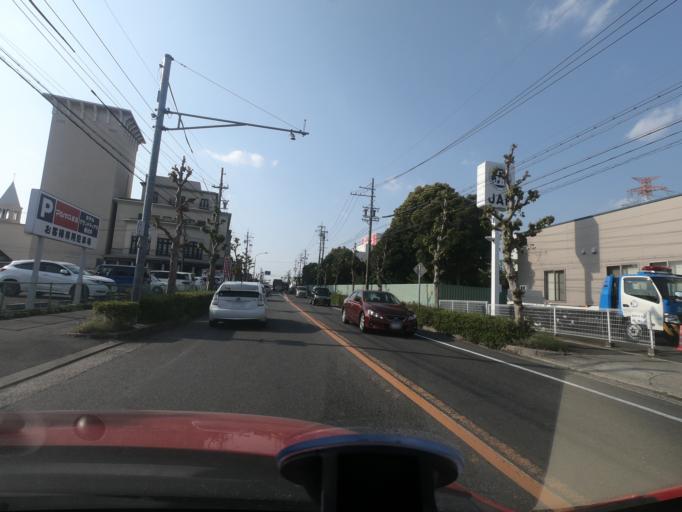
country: JP
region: Aichi
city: Kasugai
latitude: 35.2635
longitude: 136.9926
